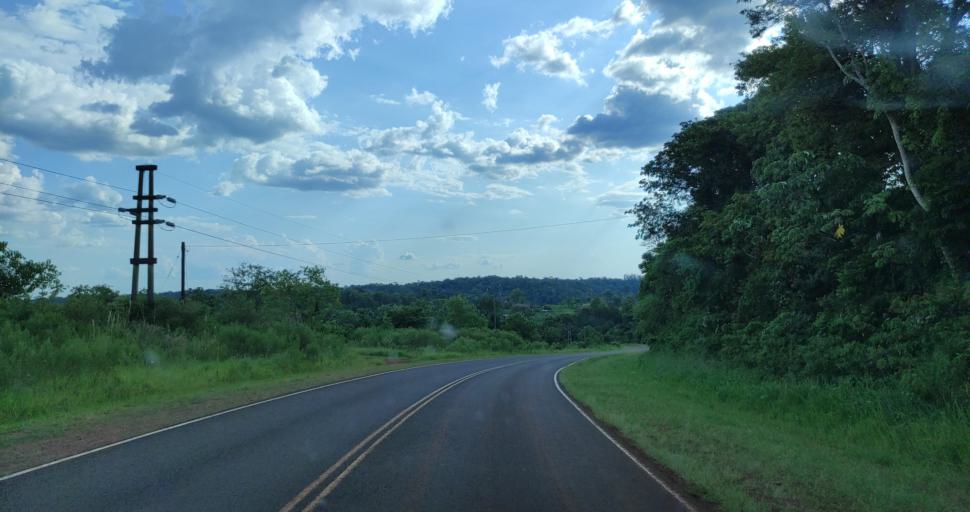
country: AR
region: Misiones
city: San Vicente
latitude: -26.3395
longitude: -54.1784
